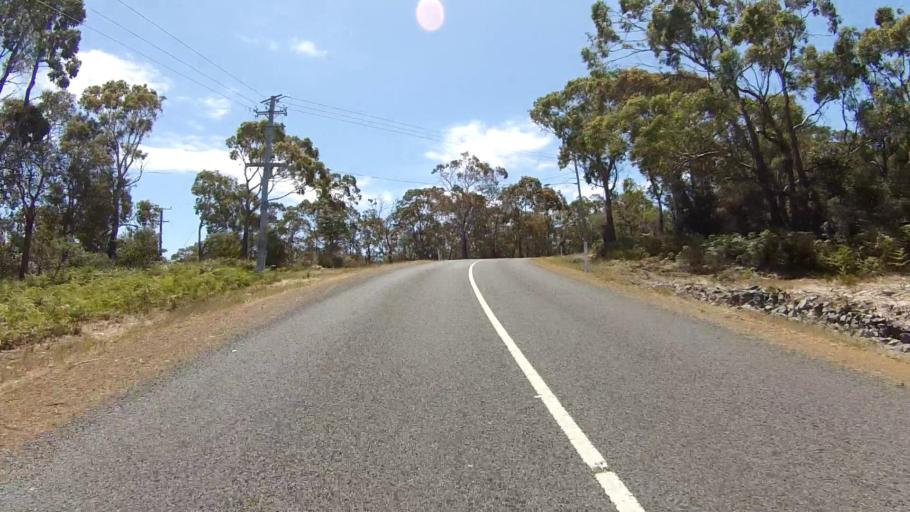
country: AU
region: Tasmania
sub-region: Clarence
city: Sandford
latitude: -43.0230
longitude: 147.4800
